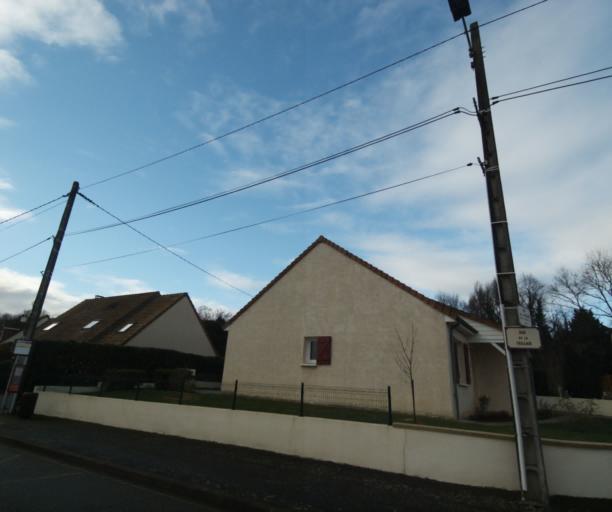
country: FR
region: Pays de la Loire
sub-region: Departement de la Sarthe
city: La Chapelle-Saint-Aubin
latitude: 48.0225
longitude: 0.1702
